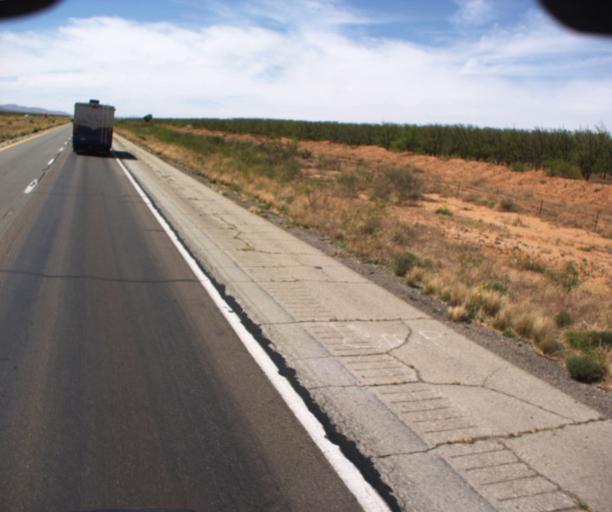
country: US
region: Arizona
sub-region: Cochise County
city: Willcox
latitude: 32.3176
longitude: -109.4656
